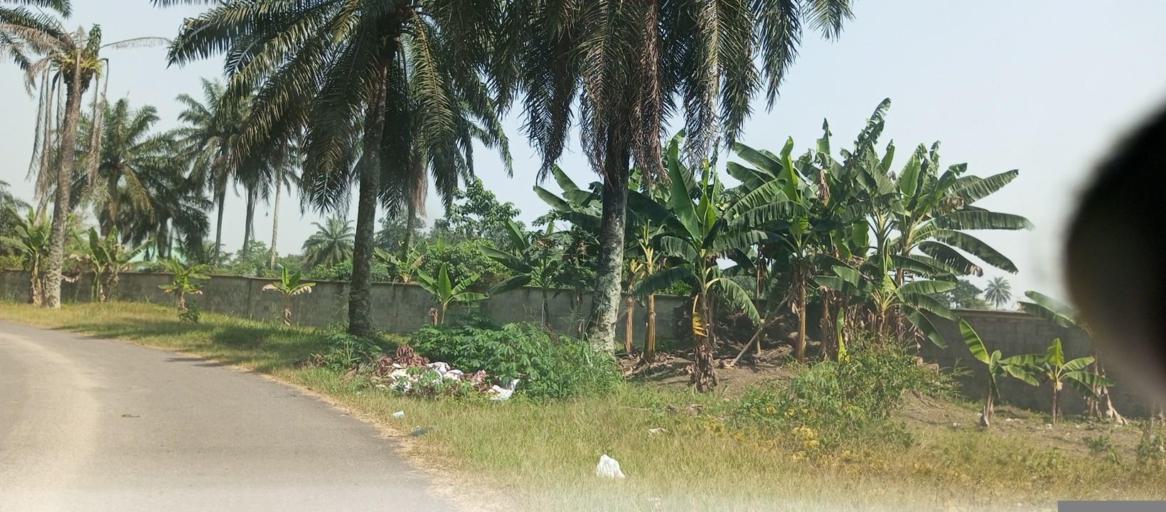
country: NG
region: Rivers
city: Emuoha
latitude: 4.9004
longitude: 6.9082
